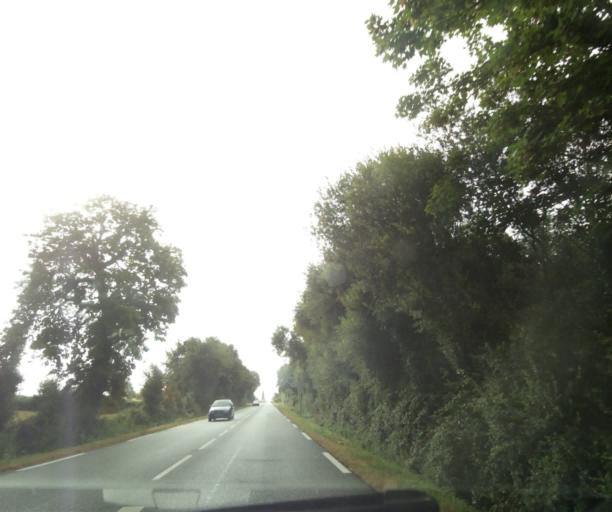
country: FR
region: Pays de la Loire
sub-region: Departement de la Vendee
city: Avrille
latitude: 46.4727
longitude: -1.5028
